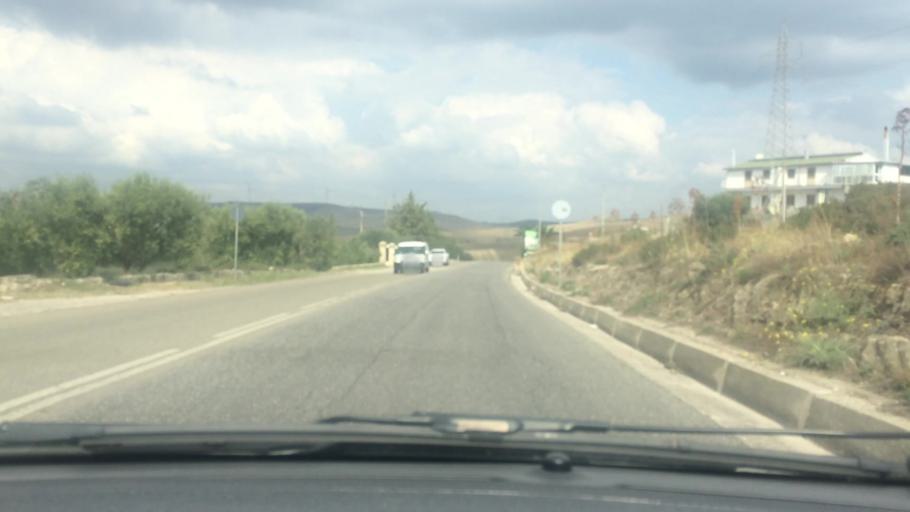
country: IT
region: Basilicate
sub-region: Provincia di Matera
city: Matera
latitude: 40.6852
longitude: 16.5703
